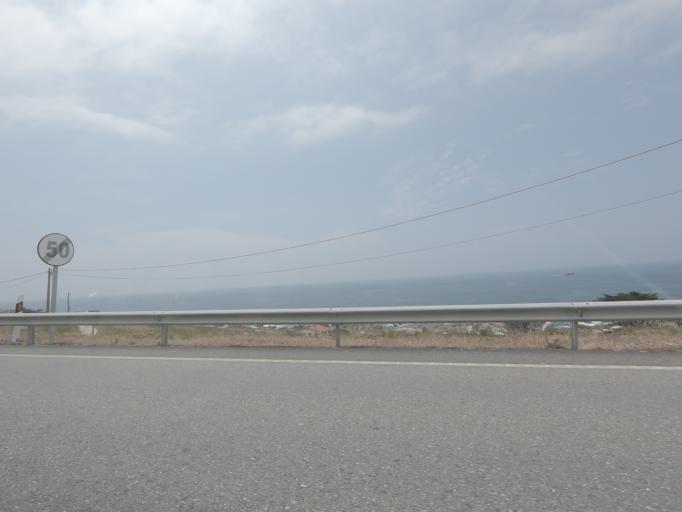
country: ES
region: Galicia
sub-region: Provincia de Pontevedra
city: O Rosal
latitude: 41.9484
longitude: -8.8829
